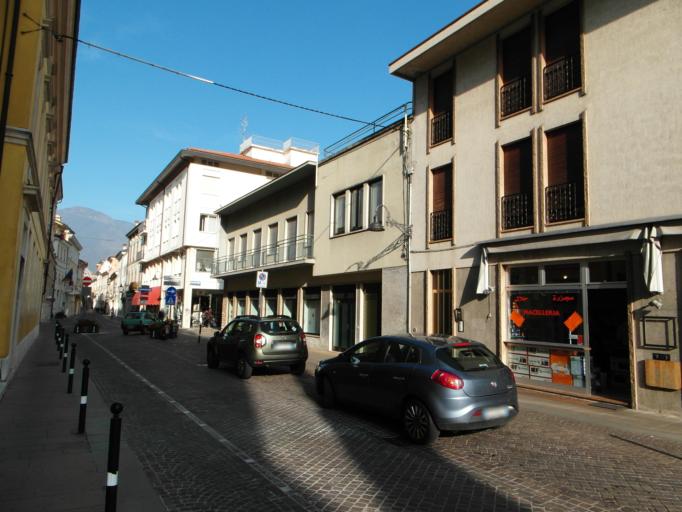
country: IT
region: Veneto
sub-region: Provincia di Vicenza
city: Schio
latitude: 45.7115
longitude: 11.3560
